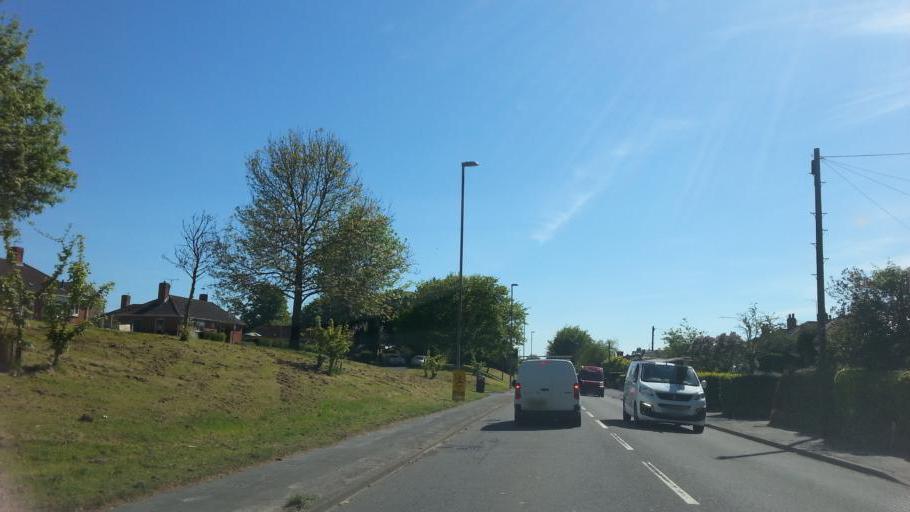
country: GB
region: England
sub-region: Dorset
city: Shaftesbury
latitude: 51.0124
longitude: -2.1913
